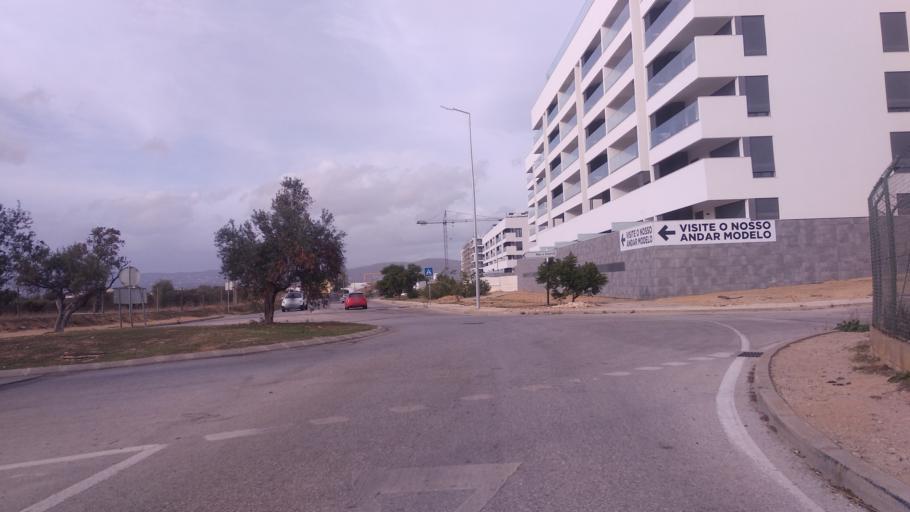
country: PT
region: Faro
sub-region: Faro
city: Faro
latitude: 37.0296
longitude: -7.9397
